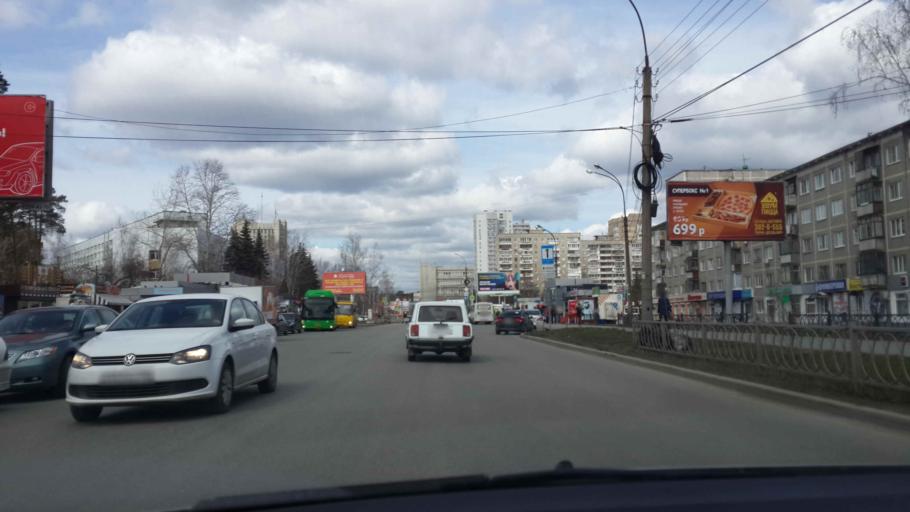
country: RU
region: Sverdlovsk
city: Sovkhoznyy
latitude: 56.8113
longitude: 60.5606
